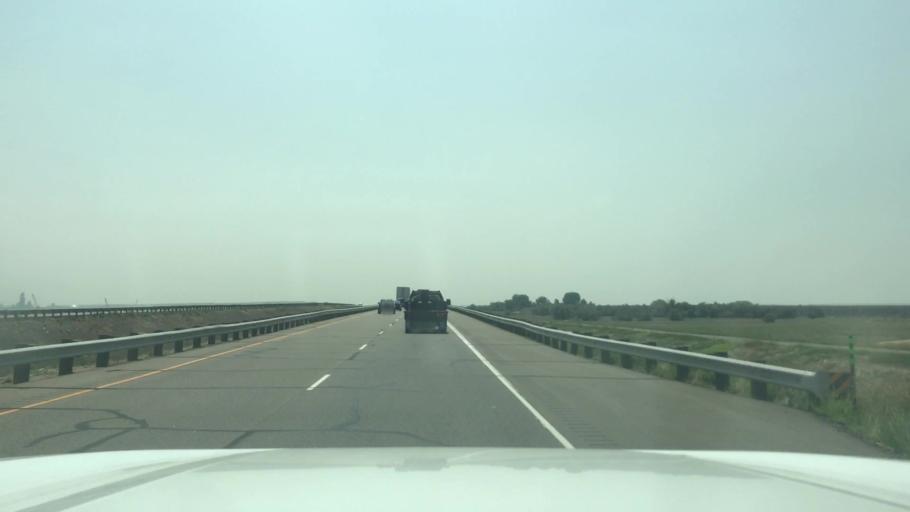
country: US
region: Colorado
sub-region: Pueblo County
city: Pueblo
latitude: 38.1868
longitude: -104.6336
